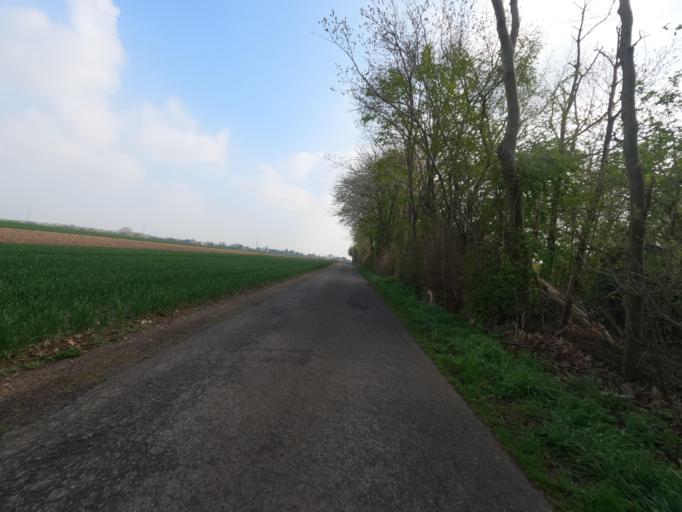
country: DE
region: North Rhine-Westphalia
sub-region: Regierungsbezirk Koln
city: Heinsberg
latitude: 51.0334
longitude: 6.0955
